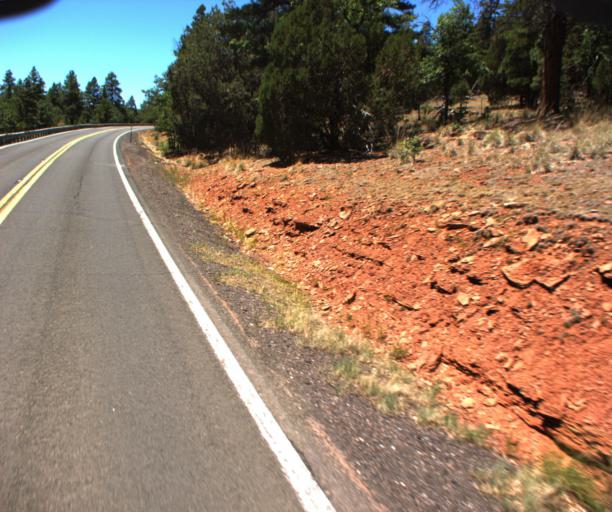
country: US
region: Arizona
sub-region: Gila County
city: Pine
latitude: 34.5972
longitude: -111.2426
